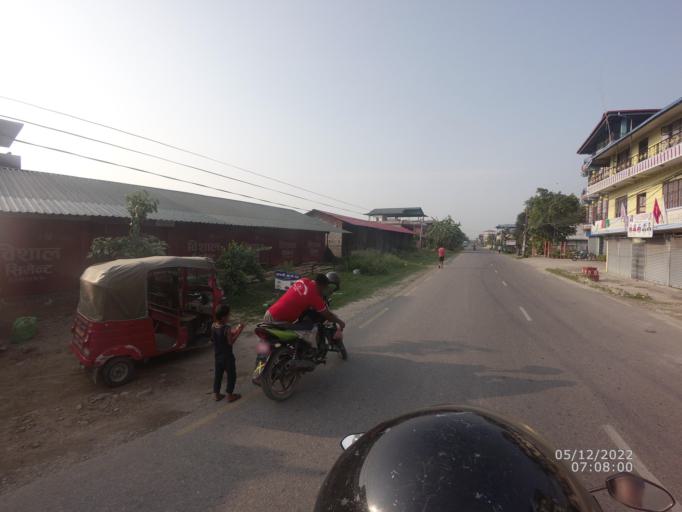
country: NP
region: Central Region
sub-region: Narayani Zone
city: Bharatpur
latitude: 27.6664
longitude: 84.4381
